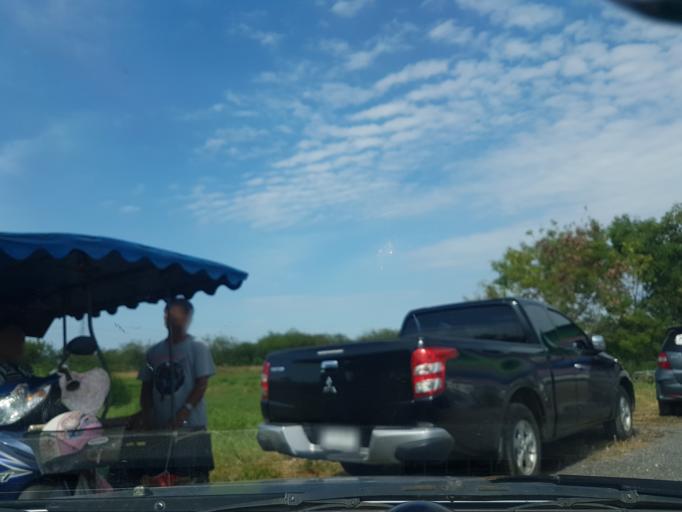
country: TH
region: Sara Buri
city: Phra Phutthabat
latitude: 14.7465
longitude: 100.7468
